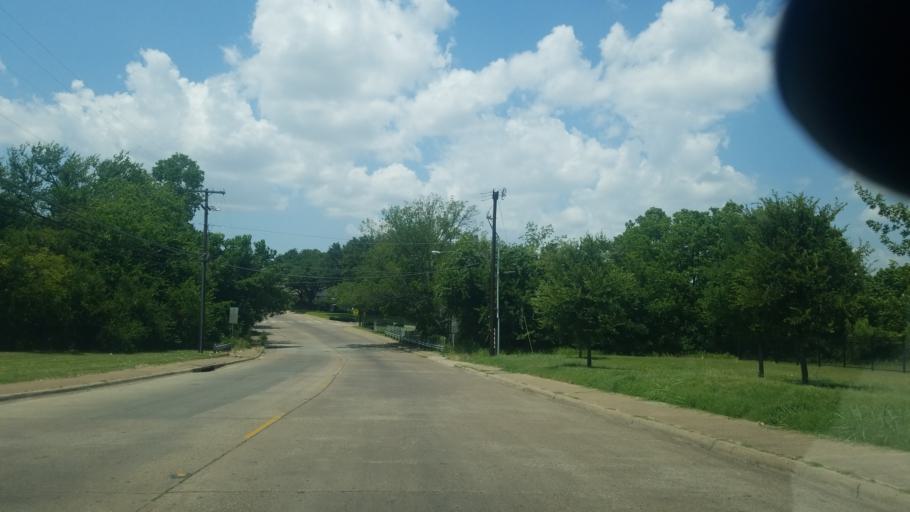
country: US
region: Texas
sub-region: Dallas County
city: Dallas
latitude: 32.7180
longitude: -96.7777
